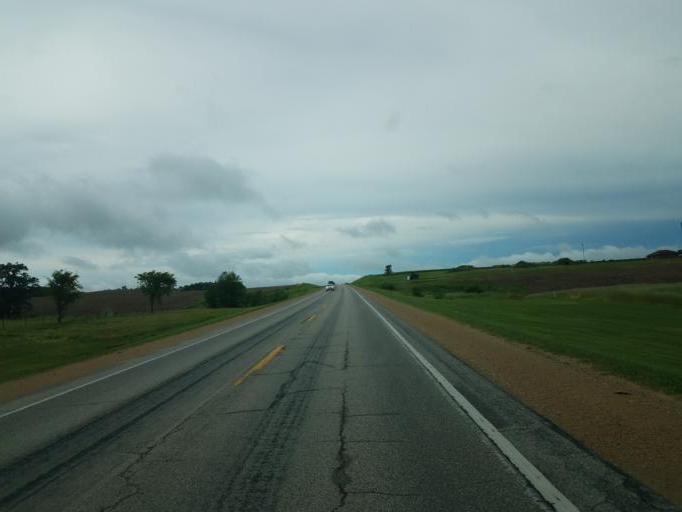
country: US
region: Wisconsin
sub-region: Vernon County
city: Hillsboro
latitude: 43.6372
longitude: -90.3572
